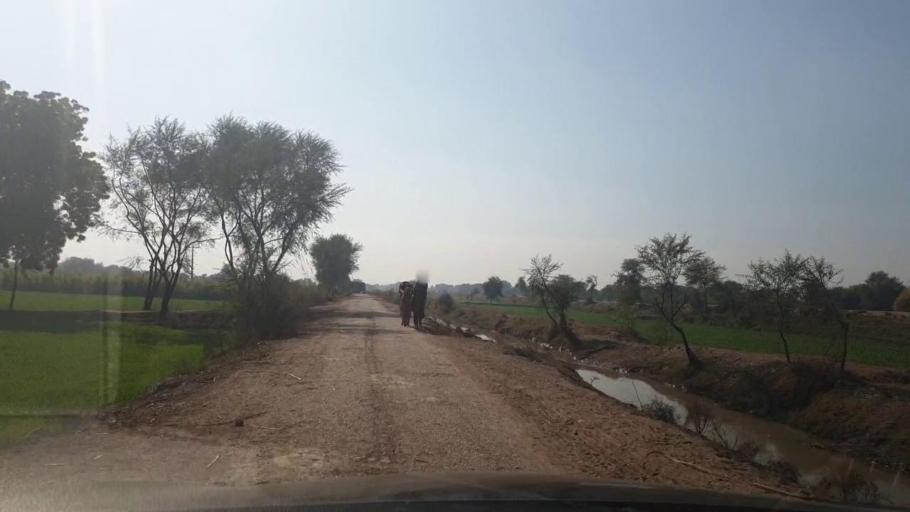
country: PK
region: Sindh
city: Ubauro
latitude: 28.1463
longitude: 69.6894
